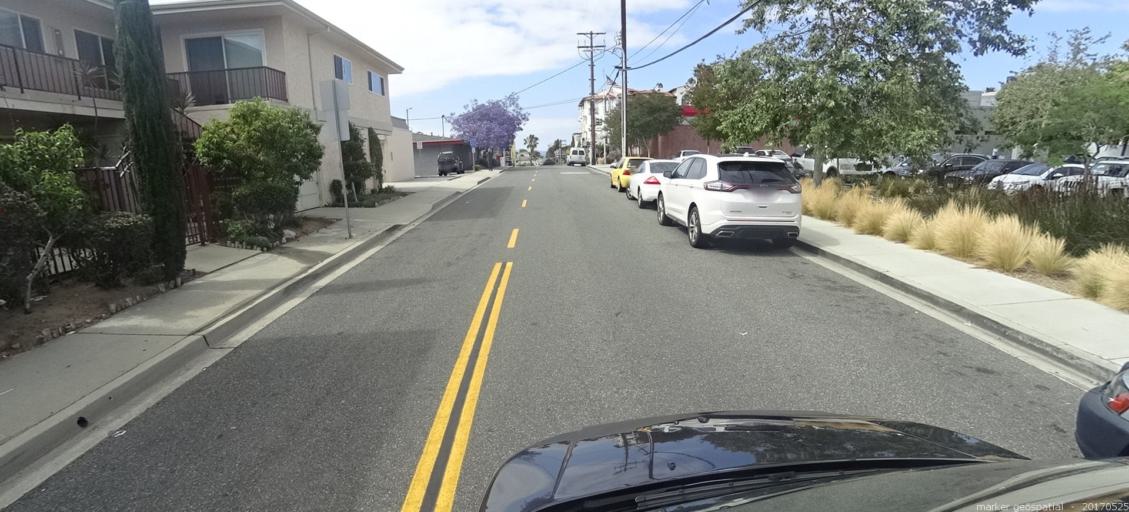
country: US
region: California
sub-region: Los Angeles County
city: Hermosa Beach
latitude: 33.8719
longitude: -118.3770
